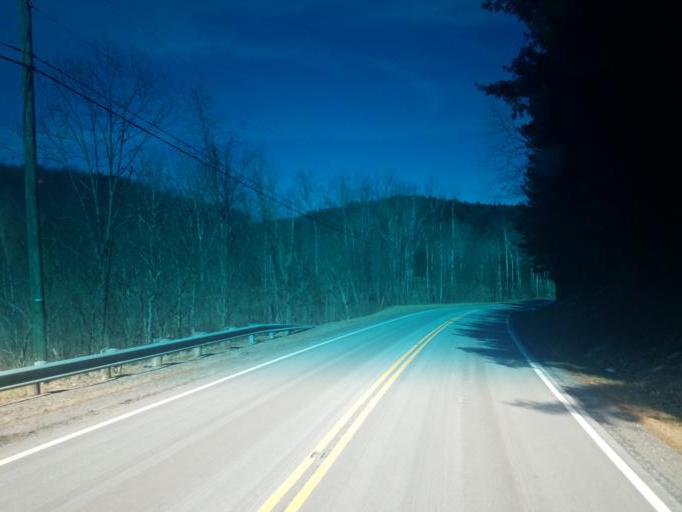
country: US
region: Ohio
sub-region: Knox County
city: Danville
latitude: 40.5246
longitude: -82.1941
